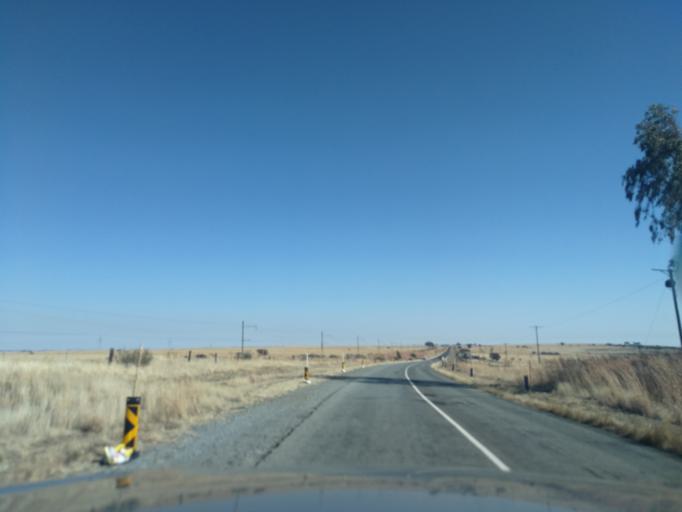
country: ZA
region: Orange Free State
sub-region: Fezile Dabi District Municipality
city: Kroonstad
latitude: -27.9018
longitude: 27.5144
